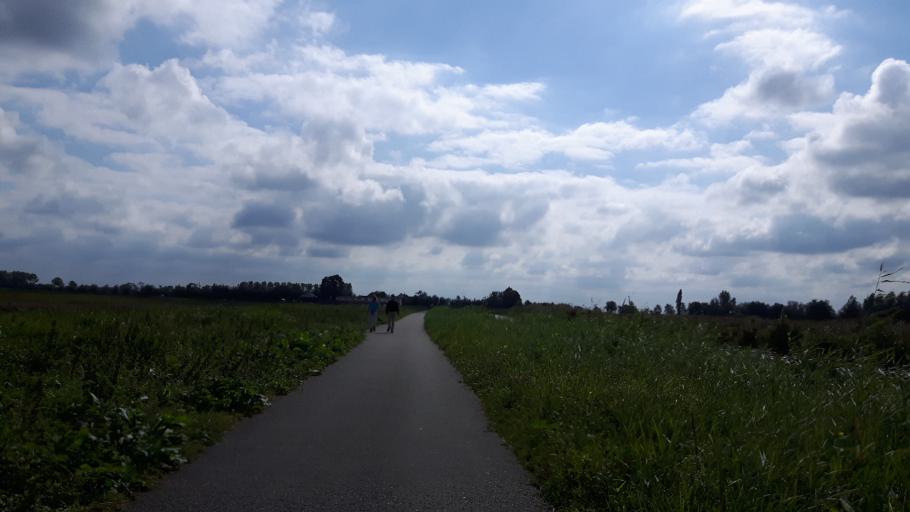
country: NL
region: South Holland
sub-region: Gemeente Nieuwkoop
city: Nieuwkoop
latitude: 52.1483
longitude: 4.8309
